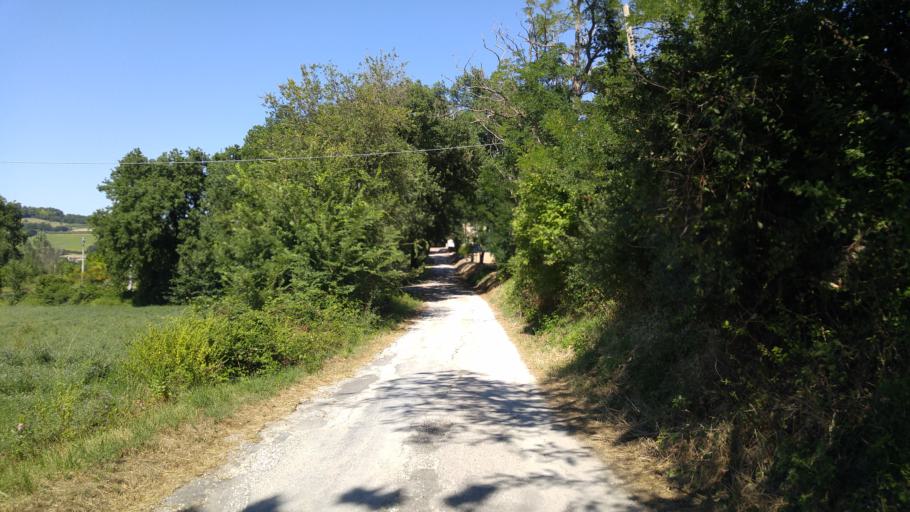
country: IT
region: The Marches
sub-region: Provincia di Pesaro e Urbino
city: Mombaroccio
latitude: 43.8322
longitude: 12.8876
